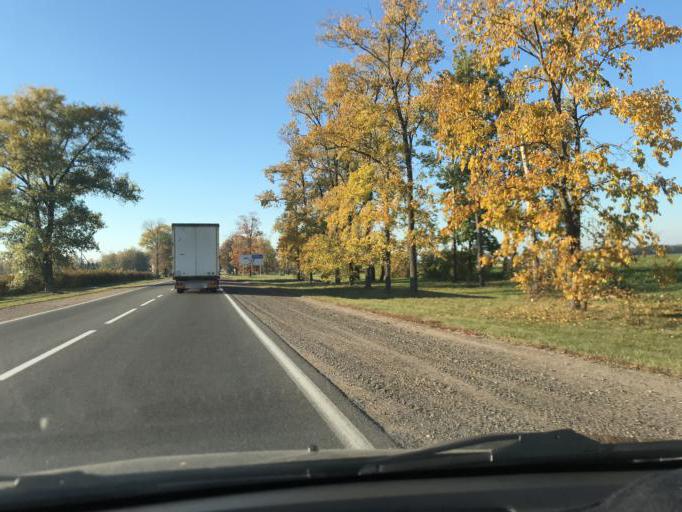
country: BY
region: Minsk
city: Slutsk
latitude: 53.0503
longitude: 27.5603
